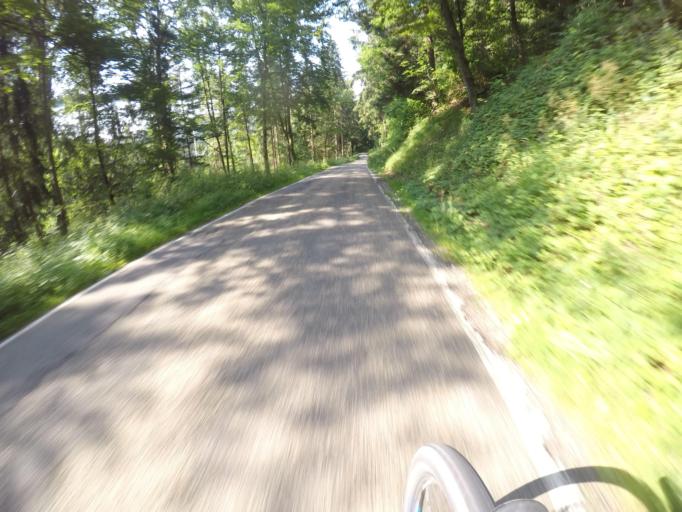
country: DE
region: Baden-Wuerttemberg
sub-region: Karlsruhe Region
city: Horb am Neckar
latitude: 48.4539
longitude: 8.7656
